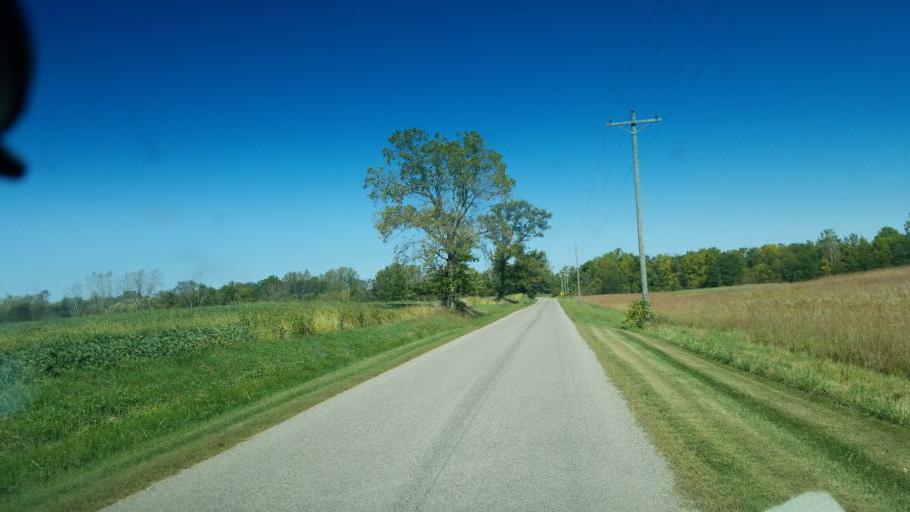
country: US
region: Ohio
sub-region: Union County
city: Richwood
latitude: 40.4758
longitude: -83.4064
